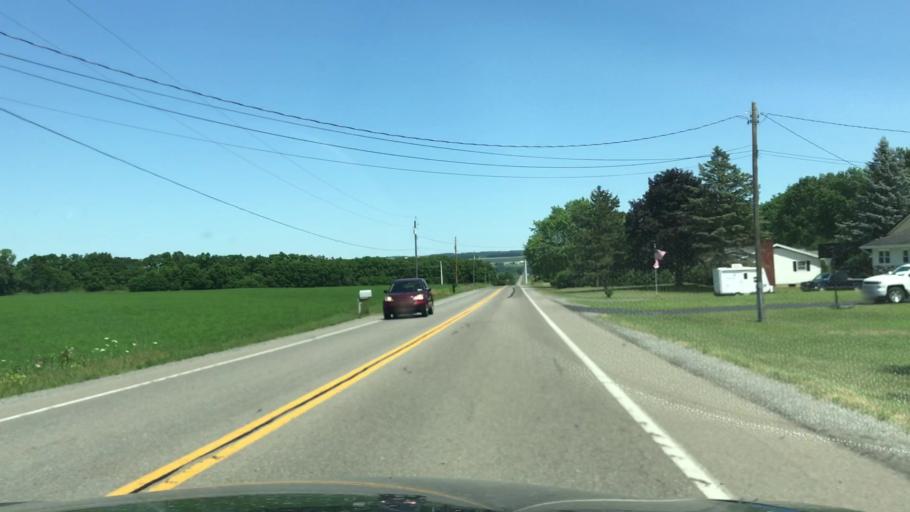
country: US
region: New York
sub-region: Livingston County
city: Mount Morris
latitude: 42.7563
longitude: -77.8909
